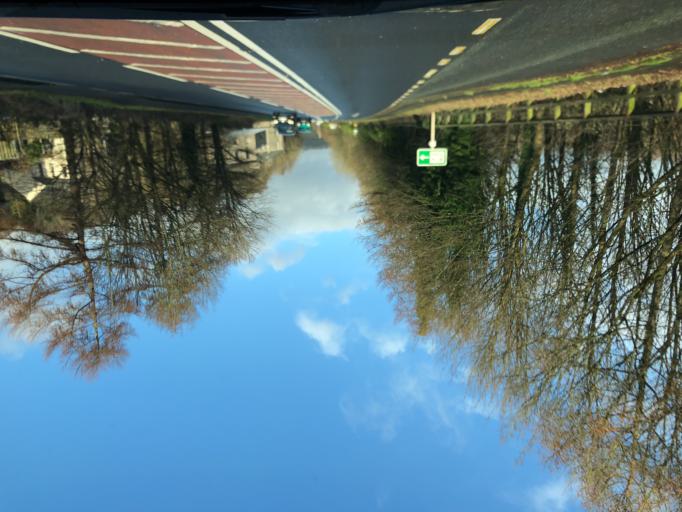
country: GB
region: England
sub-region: Cumbria
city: Grange-over-Sands
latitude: 54.2539
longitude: -2.9886
